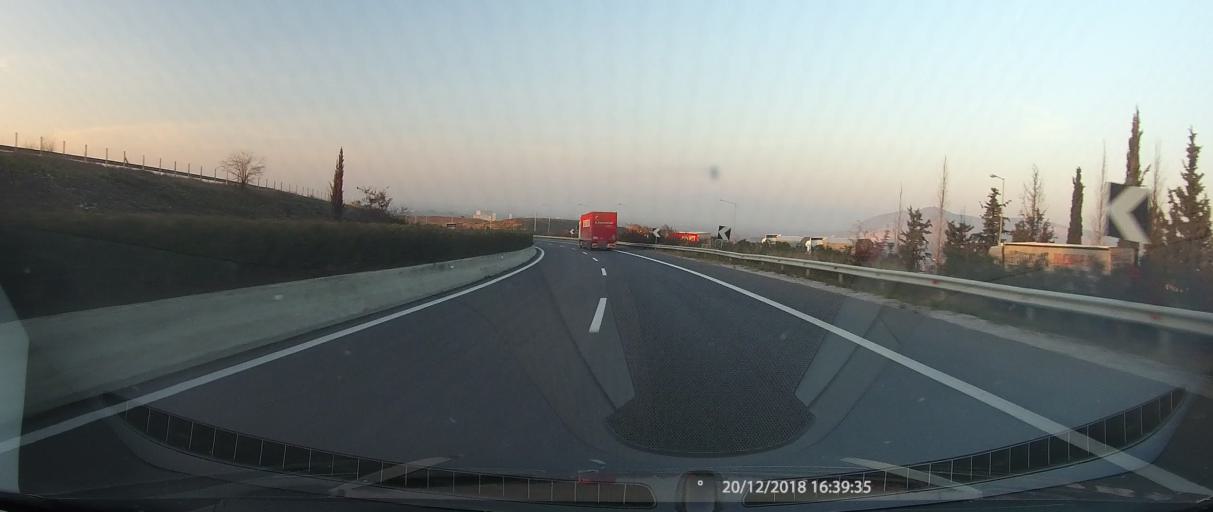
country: GR
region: Thessaly
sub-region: Nomos Magnisias
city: Velestino
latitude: 39.3607
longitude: 22.7739
